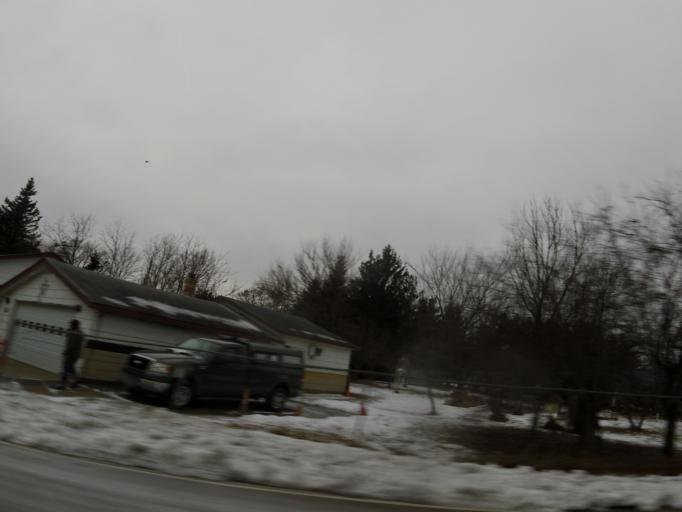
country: US
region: Minnesota
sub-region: Scott County
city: Jordan
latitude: 44.6778
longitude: -93.6398
